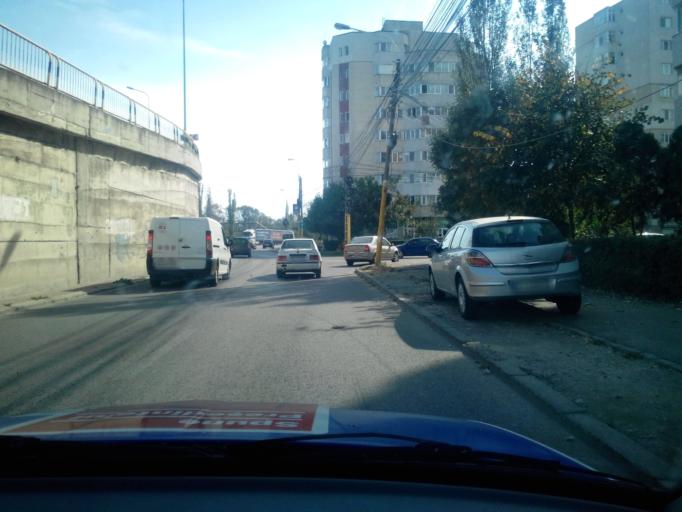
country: RO
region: Constanta
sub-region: Municipiul Constanta
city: Constanta
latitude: 44.1510
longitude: 28.6237
